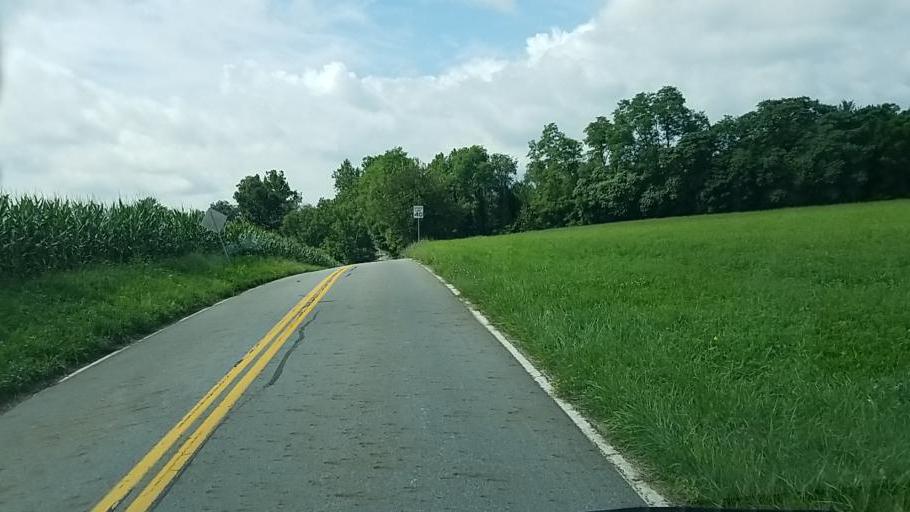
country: US
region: Pennsylvania
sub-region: Dauphin County
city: Elizabethville
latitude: 40.5939
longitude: -76.8826
